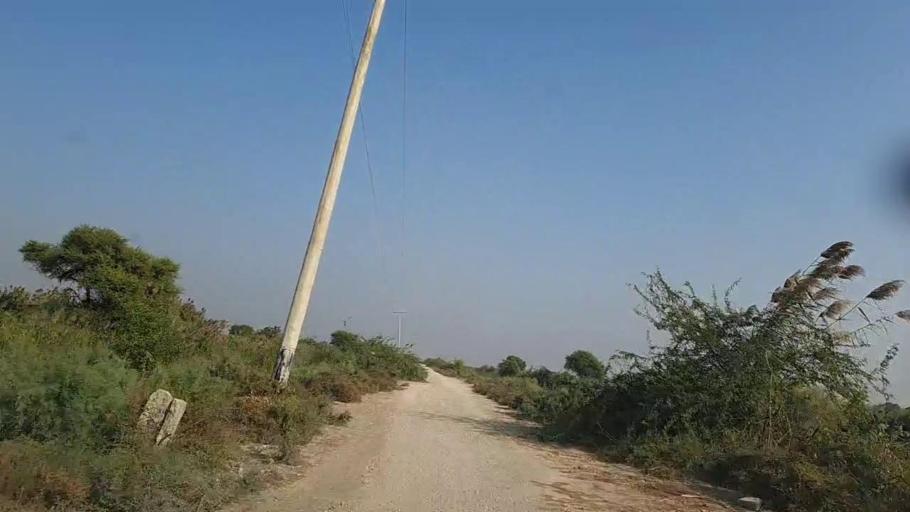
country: PK
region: Sindh
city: Jati
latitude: 24.4602
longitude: 68.3054
